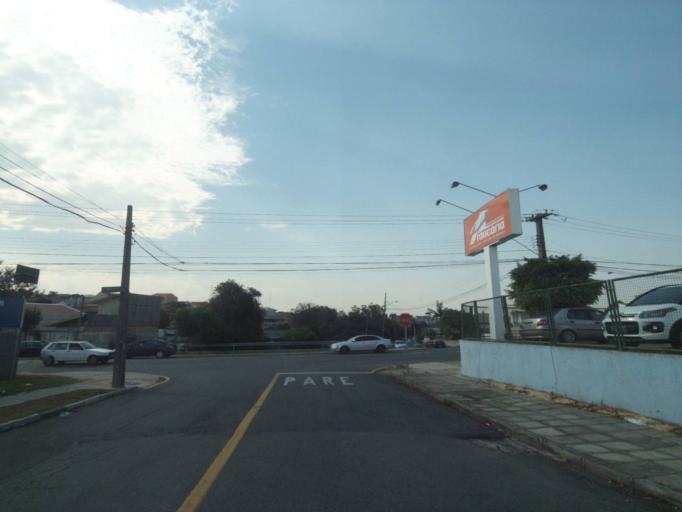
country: BR
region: Parana
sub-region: Sao Jose Dos Pinhais
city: Sao Jose dos Pinhais
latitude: -25.5034
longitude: -49.2588
